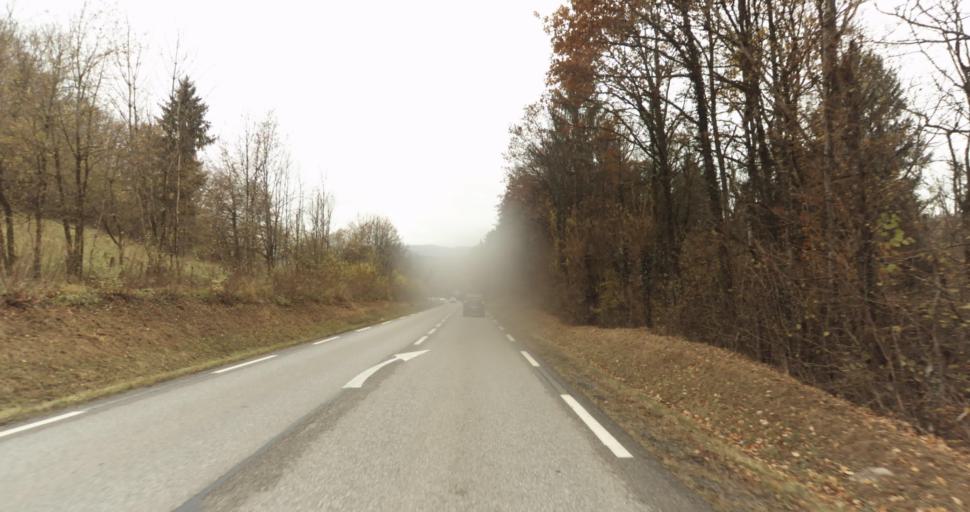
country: FR
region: Rhone-Alpes
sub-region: Departement de la Haute-Savoie
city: Groisy
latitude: 46.0060
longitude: 6.1924
